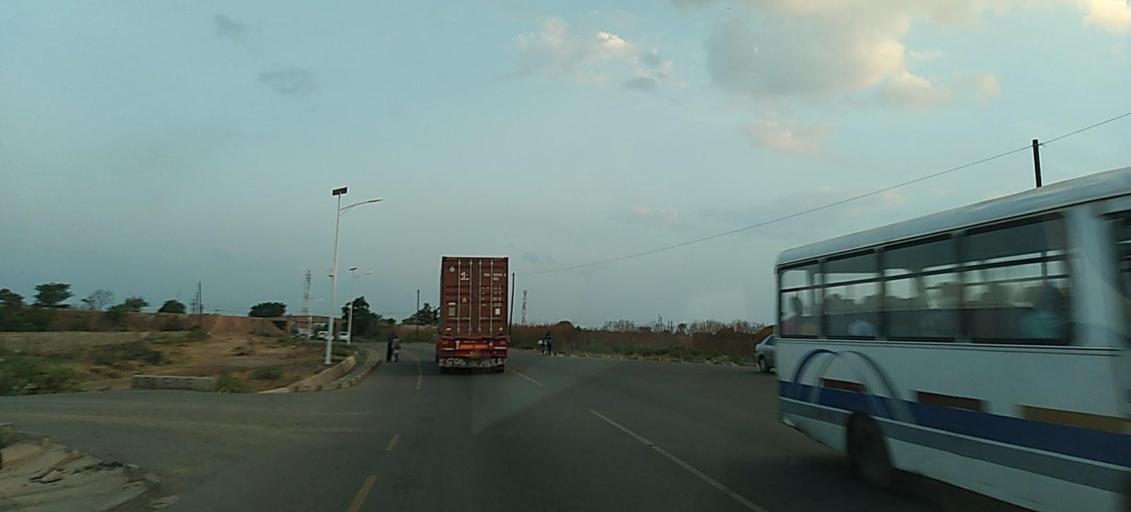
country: ZM
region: Copperbelt
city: Chingola
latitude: -12.5389
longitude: 27.8404
